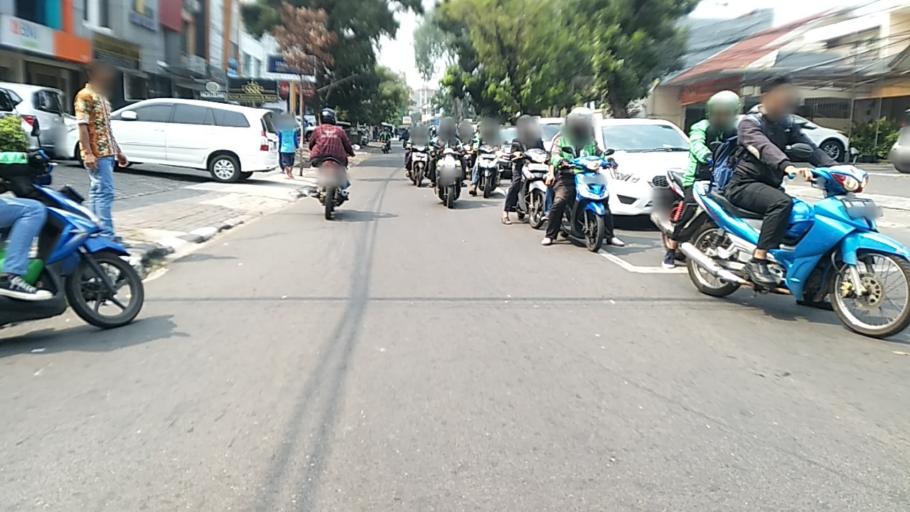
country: ID
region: Jakarta Raya
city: Jakarta
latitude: -6.2297
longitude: 106.8497
